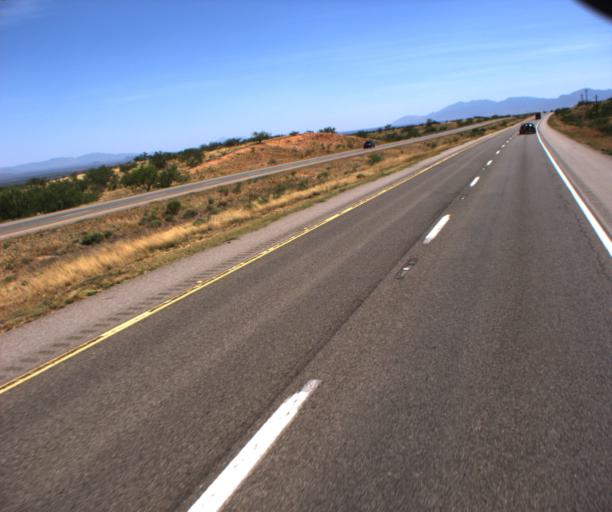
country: US
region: Arizona
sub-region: Cochise County
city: Whetstone
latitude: 31.8526
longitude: -110.3414
